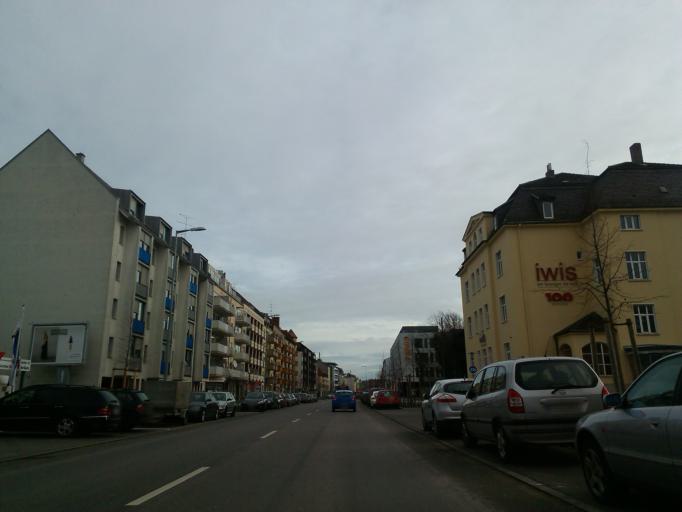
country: DE
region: Bavaria
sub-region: Upper Bavaria
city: Munich
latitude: 48.1168
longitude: 11.5292
